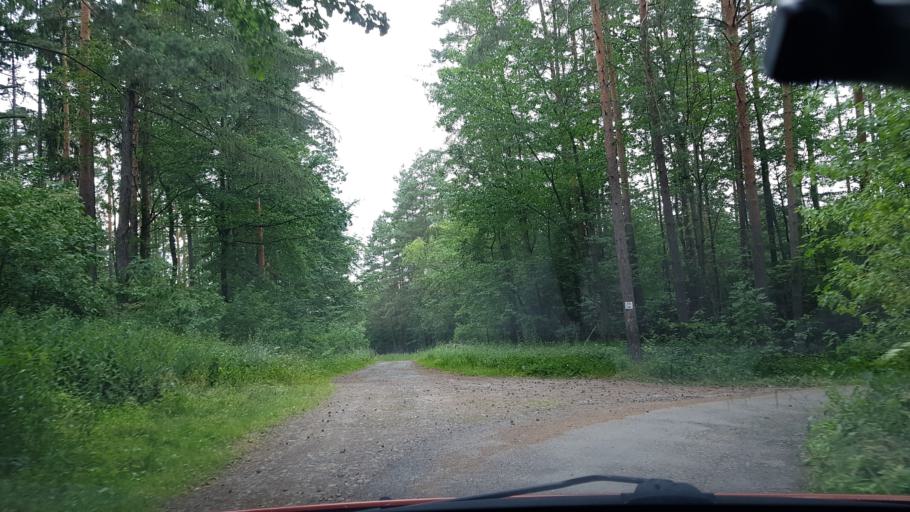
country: PL
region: Lower Silesian Voivodeship
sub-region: Powiat zabkowicki
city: Stoszowice
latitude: 50.5637
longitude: 16.7450
